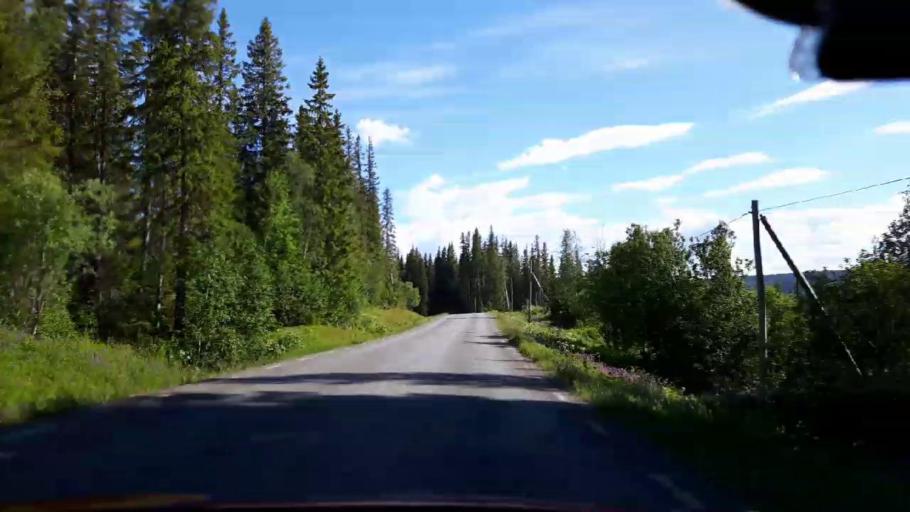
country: SE
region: Jaemtland
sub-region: Krokoms Kommun
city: Valla
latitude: 63.7131
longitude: 14.1366
